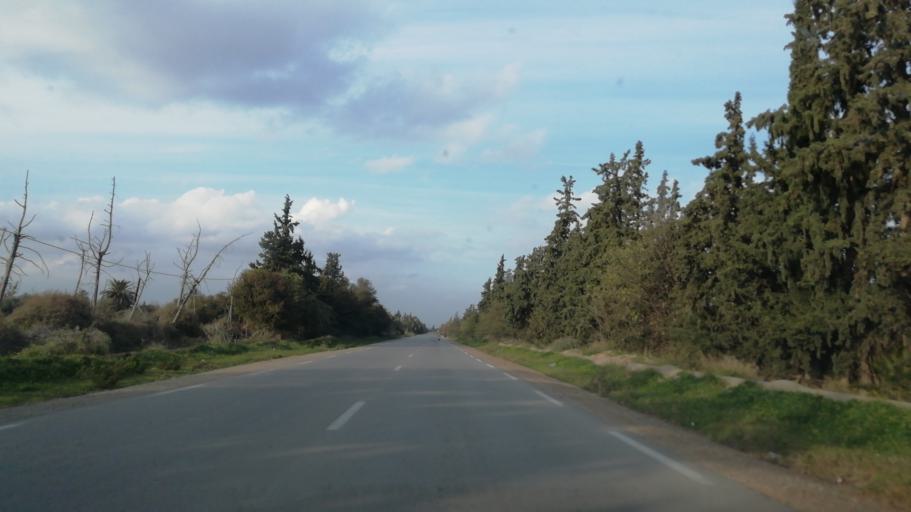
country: DZ
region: Mascara
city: Mascara
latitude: 35.6073
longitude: 0.0523
